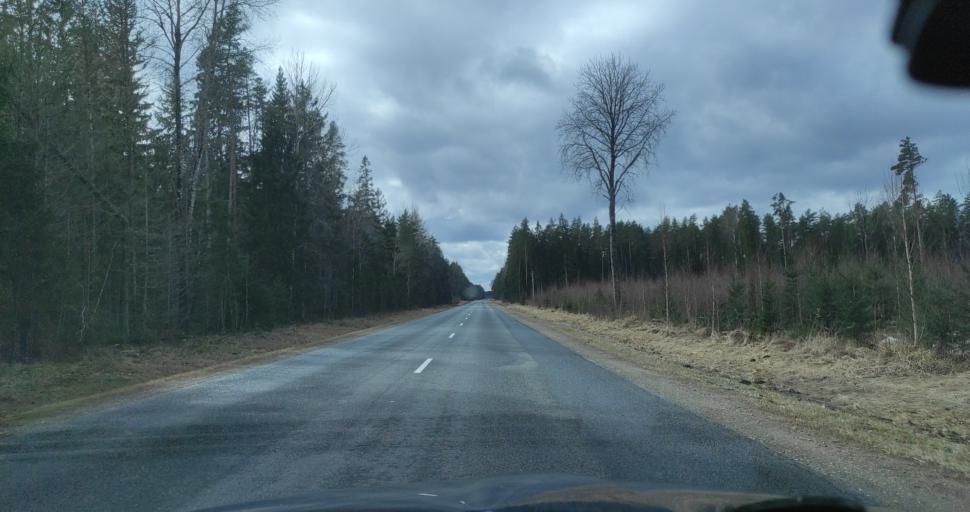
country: LV
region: Talsu Rajons
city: Stende
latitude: 57.1164
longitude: 22.5130
